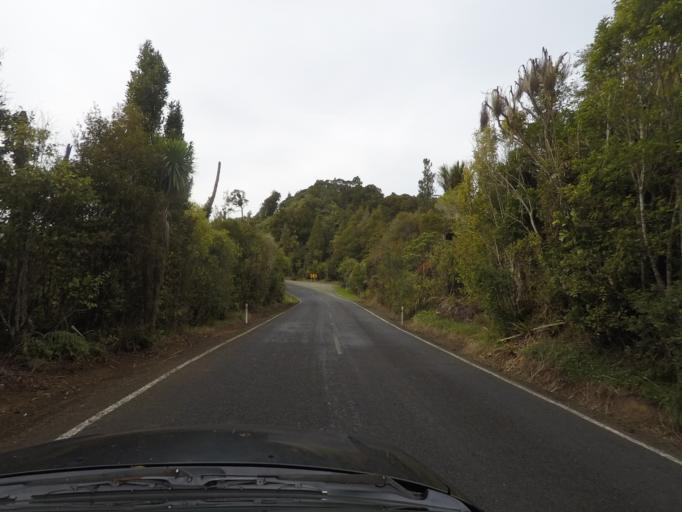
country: NZ
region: Auckland
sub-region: Auckland
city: Titirangi
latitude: -36.9424
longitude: 174.5928
